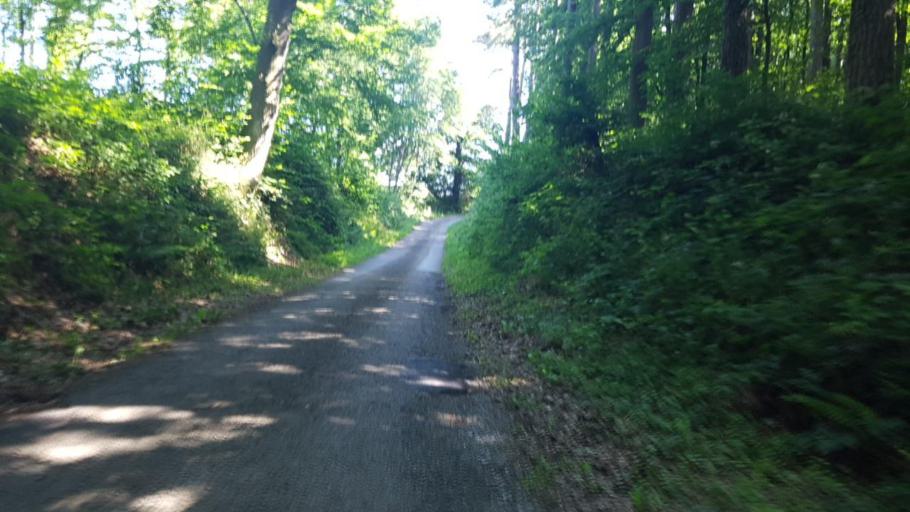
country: BE
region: Wallonia
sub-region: Province du Hainaut
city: Momignies
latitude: 50.0038
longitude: 4.1380
